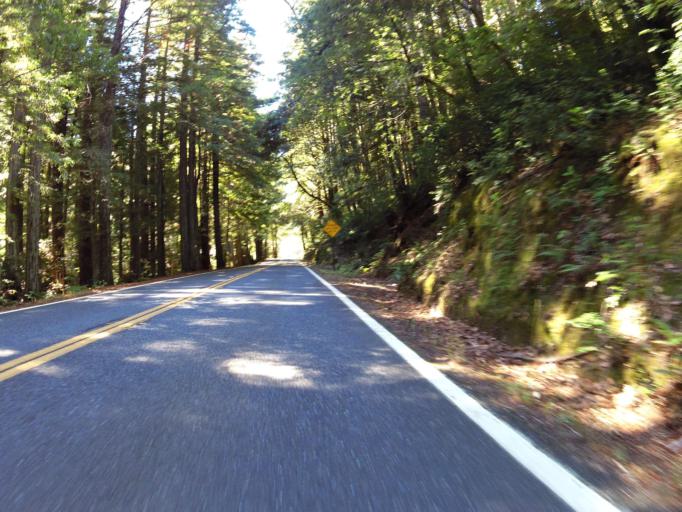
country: US
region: California
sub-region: Humboldt County
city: Redway
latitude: 39.8169
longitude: -123.7836
